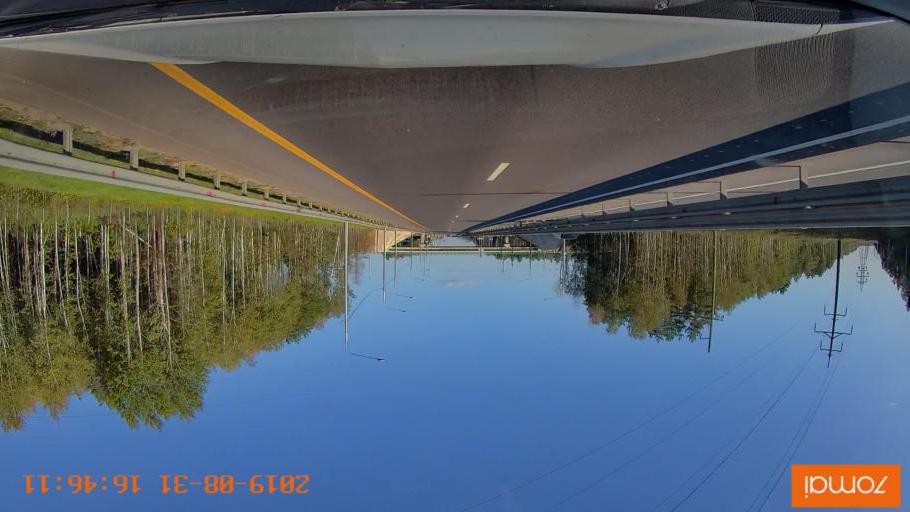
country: RU
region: Kaluga
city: Mstikhino
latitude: 54.6315
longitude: 36.1289
